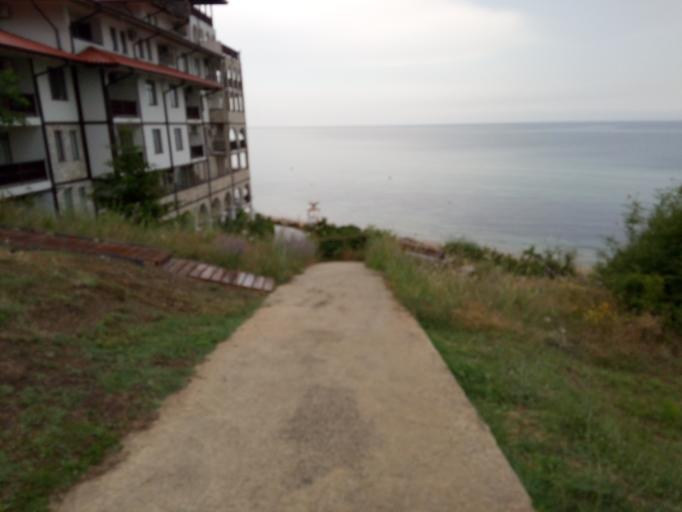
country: BG
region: Burgas
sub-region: Obshtina Nesebur
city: Sveti Vlas
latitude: 42.7057
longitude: 27.7758
